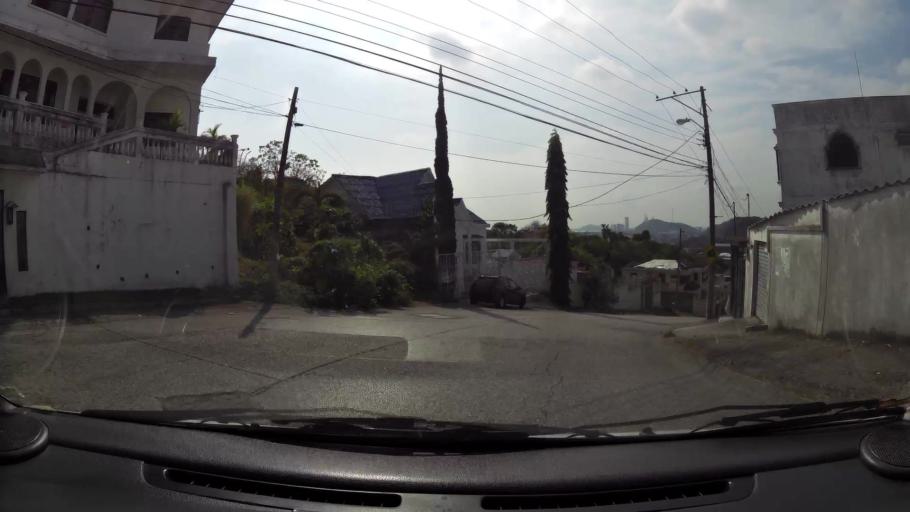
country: EC
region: Guayas
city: Guayaquil
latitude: -2.1787
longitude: -79.9137
